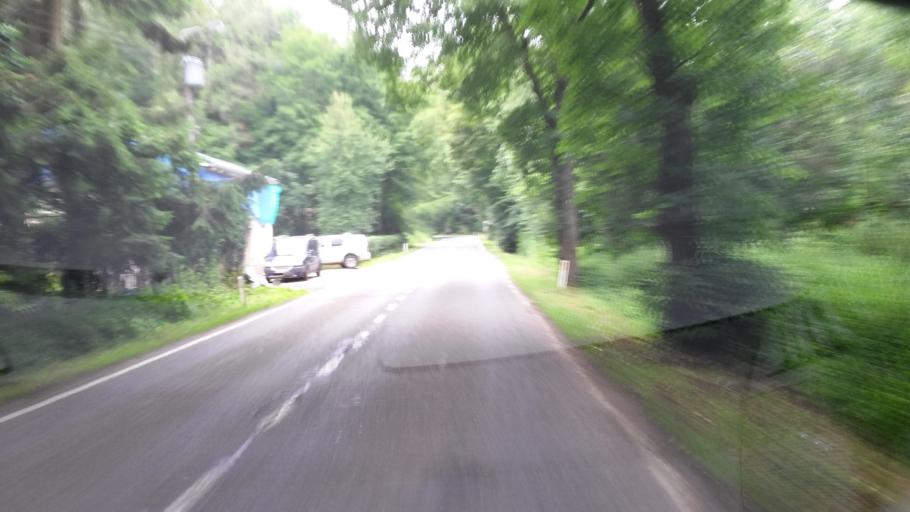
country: LU
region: Luxembourg
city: Eischen
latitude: 49.6954
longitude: 5.8634
